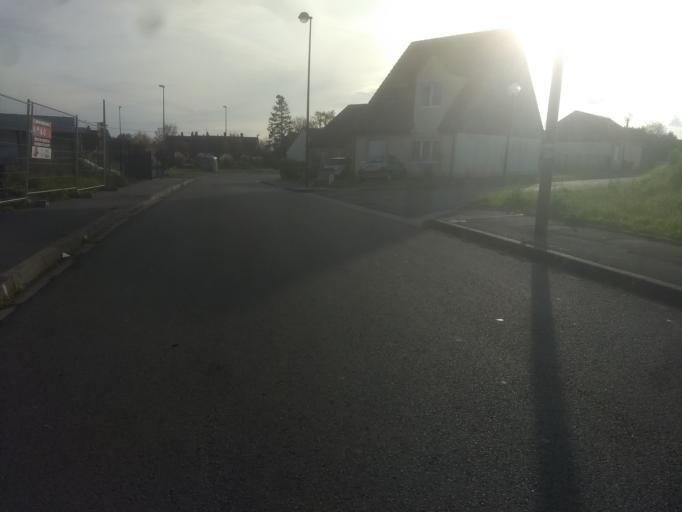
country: FR
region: Nord-Pas-de-Calais
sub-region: Departement du Pas-de-Calais
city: Arras
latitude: 50.2780
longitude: 2.7779
